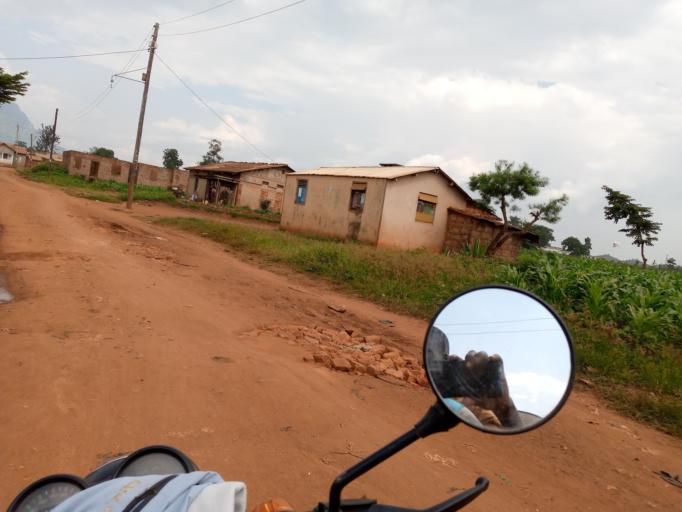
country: UG
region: Eastern Region
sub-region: Mbale District
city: Mbale
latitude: 1.0823
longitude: 34.1590
